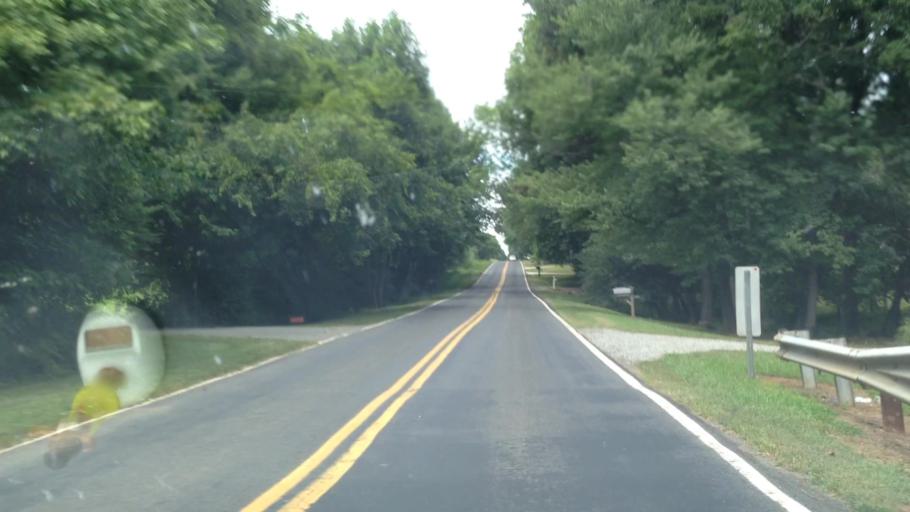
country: US
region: North Carolina
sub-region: Forsyth County
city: Walkertown
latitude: 36.2148
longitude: -80.1133
